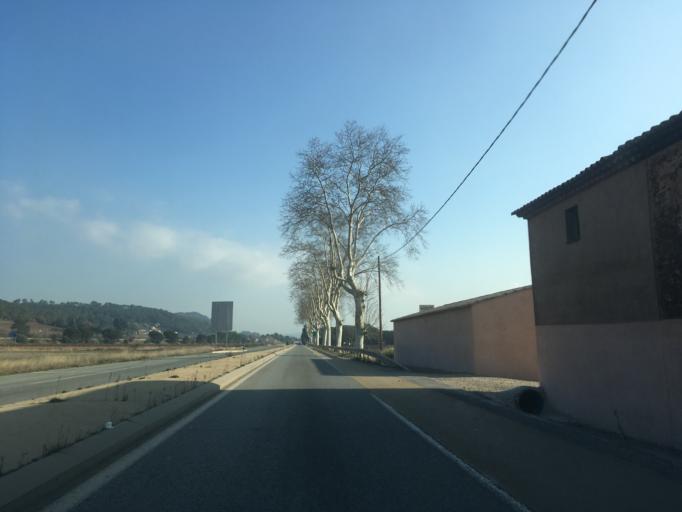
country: FR
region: Provence-Alpes-Cote d'Azur
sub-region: Departement du Var
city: Le Cannet-des-Maures
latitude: 43.3991
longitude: 6.3673
